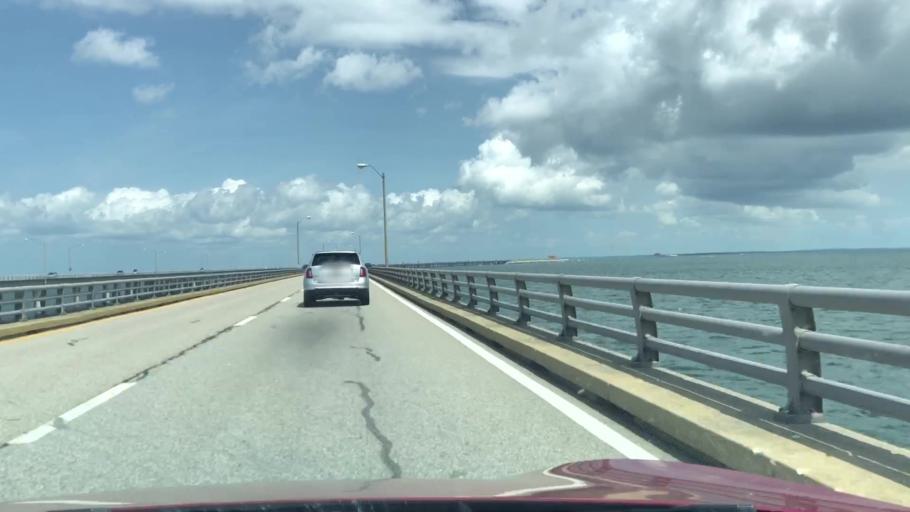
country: US
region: Virginia
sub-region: City of Virginia Beach
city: Virginia Beach
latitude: 37.0161
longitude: -76.0920
